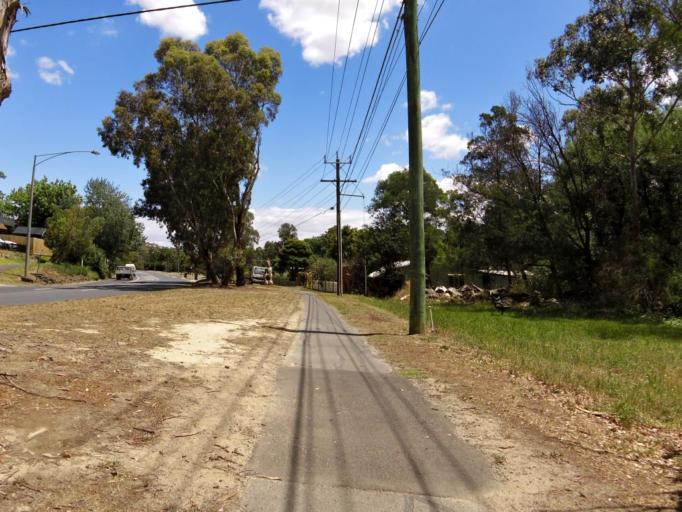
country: AU
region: Victoria
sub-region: Nillumbik
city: Eltham North
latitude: -37.7028
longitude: 145.1633
